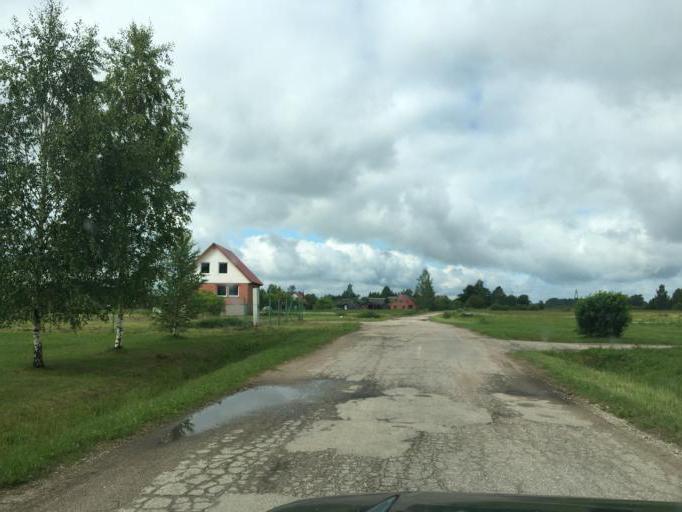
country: LV
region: Balvu Rajons
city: Balvi
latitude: 57.2136
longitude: 27.3177
